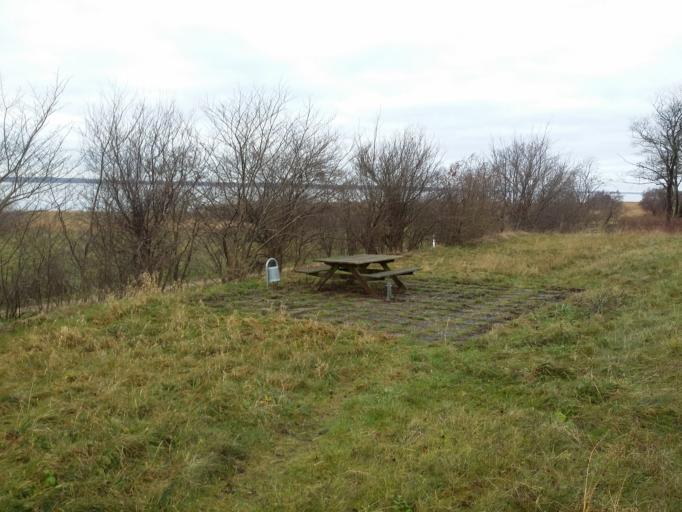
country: DK
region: Capital Region
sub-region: Frederikssund Kommune
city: Frederikssund
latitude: 55.8649
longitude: 12.0680
